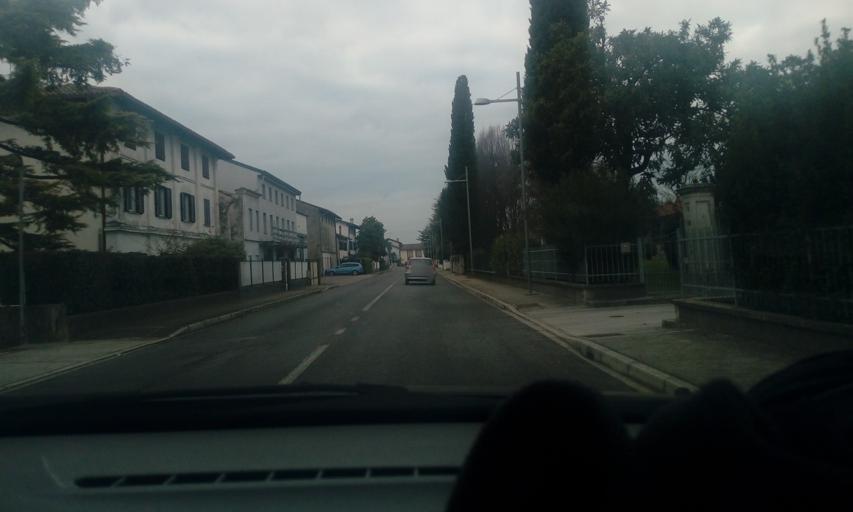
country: IT
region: Friuli Venezia Giulia
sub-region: Provincia di Udine
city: Campolongo al Torre-Cavenzano
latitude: 45.8629
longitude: 13.3907
